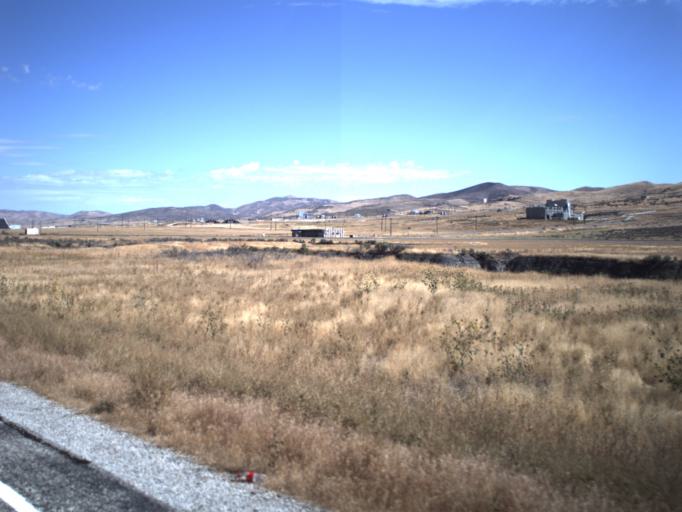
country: US
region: Utah
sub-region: Box Elder County
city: Tremonton
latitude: 41.6888
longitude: -112.4440
